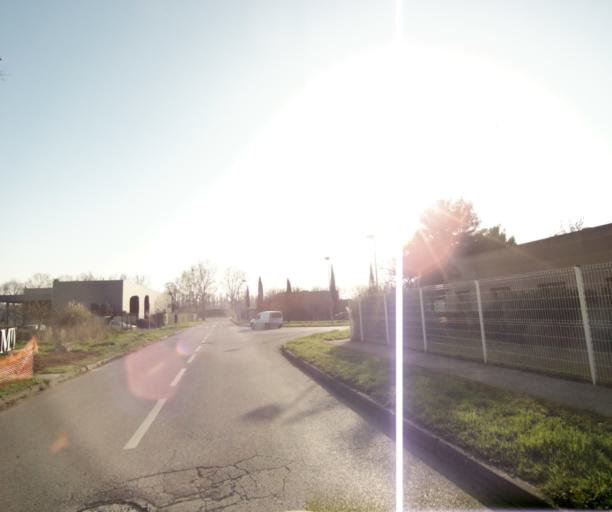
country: FR
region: Provence-Alpes-Cote d'Azur
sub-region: Departement des Bouches-du-Rhone
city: Saint-Victoret
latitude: 43.4246
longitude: 5.2595
